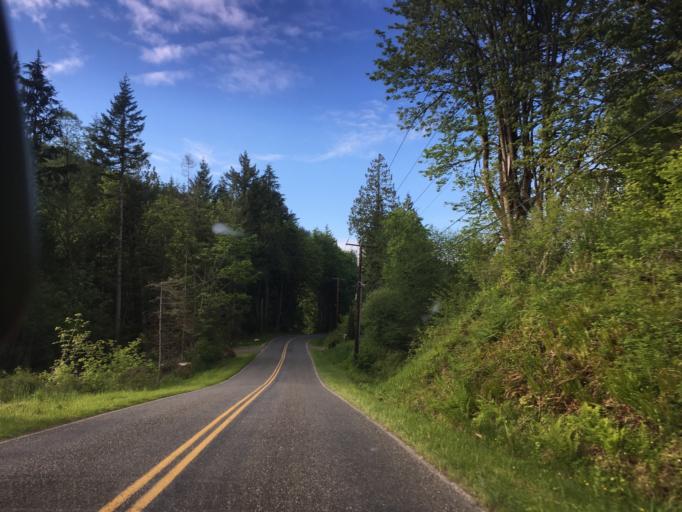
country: US
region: Washington
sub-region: Whatcom County
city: Sudden Valley
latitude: 48.7731
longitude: -122.3553
